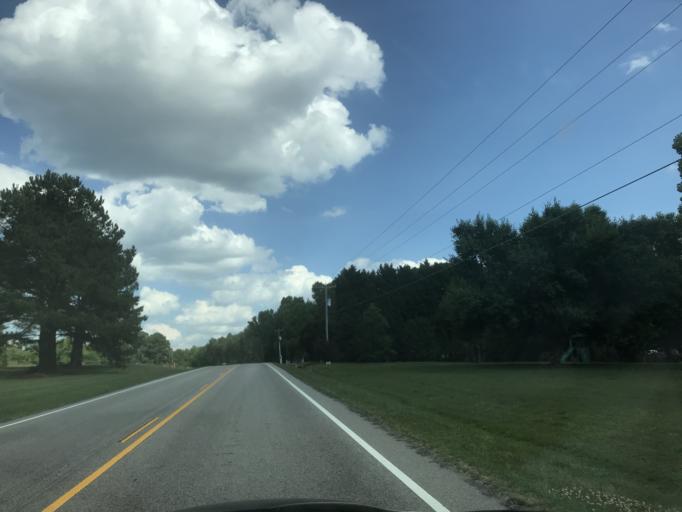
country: US
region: North Carolina
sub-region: Wake County
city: Zebulon
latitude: 35.9596
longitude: -78.2779
